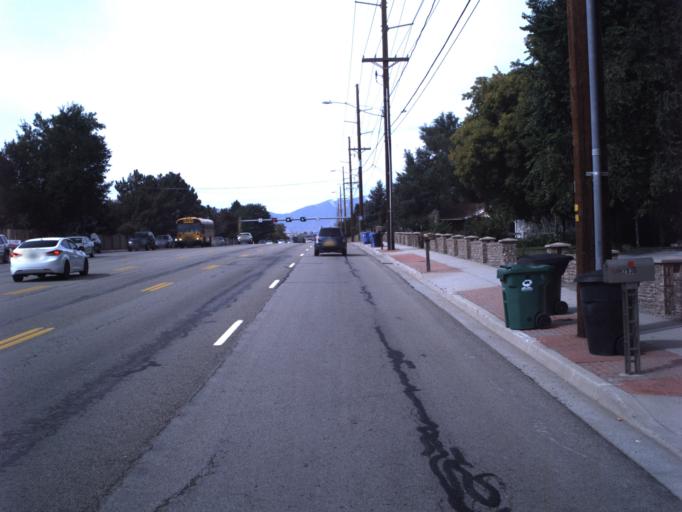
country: US
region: Utah
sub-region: Salt Lake County
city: Taylorsville
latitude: 40.6532
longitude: -111.9601
